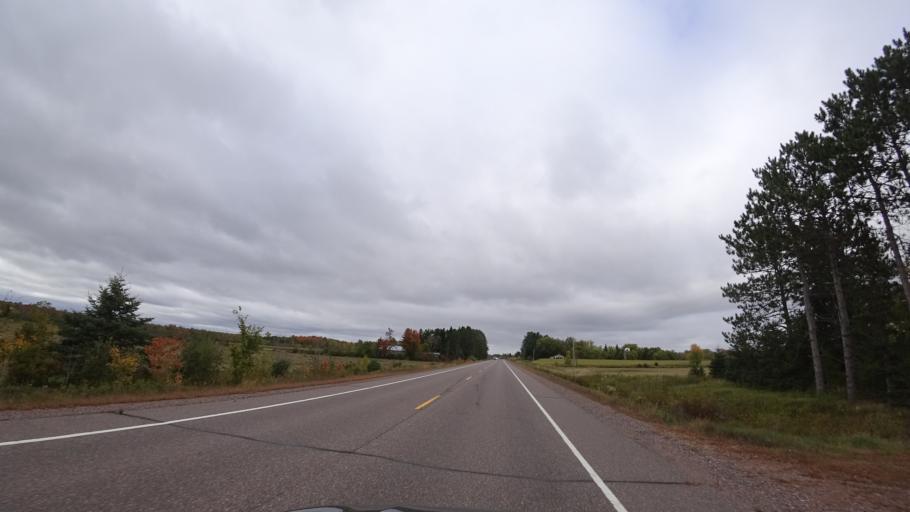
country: US
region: Wisconsin
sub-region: Rusk County
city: Ladysmith
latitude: 45.5394
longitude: -91.1114
